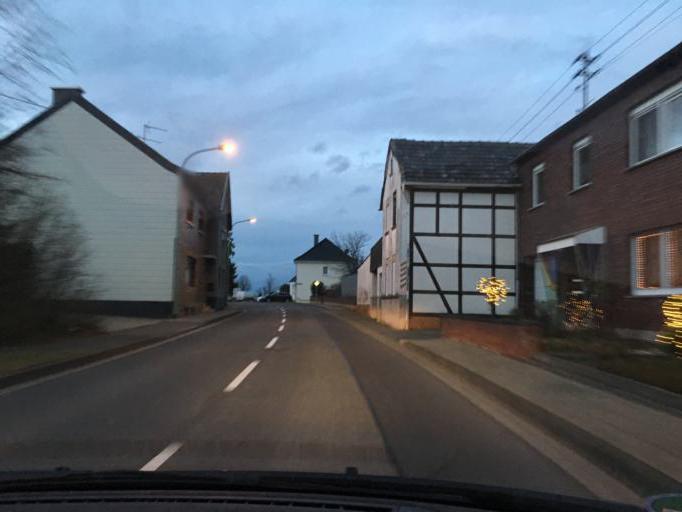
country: DE
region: North Rhine-Westphalia
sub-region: Regierungsbezirk Koln
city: Vettweiss
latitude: 50.7136
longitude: 6.5697
